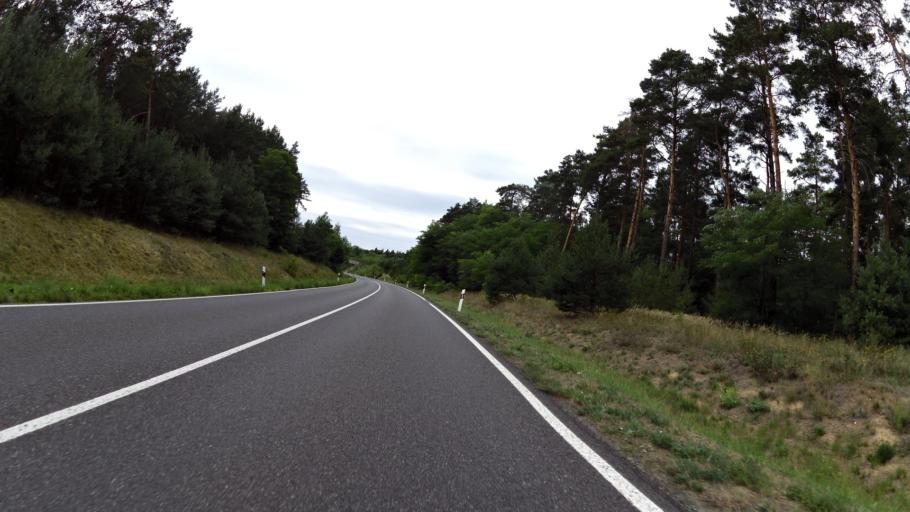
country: DE
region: Brandenburg
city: Schenkendobern
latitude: 51.8986
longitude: 14.6040
